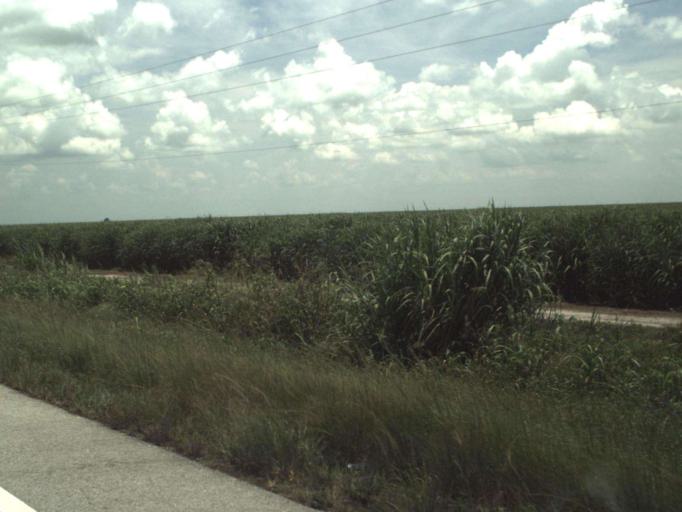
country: US
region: Florida
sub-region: Palm Beach County
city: Pahokee
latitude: 26.8326
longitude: -80.5897
